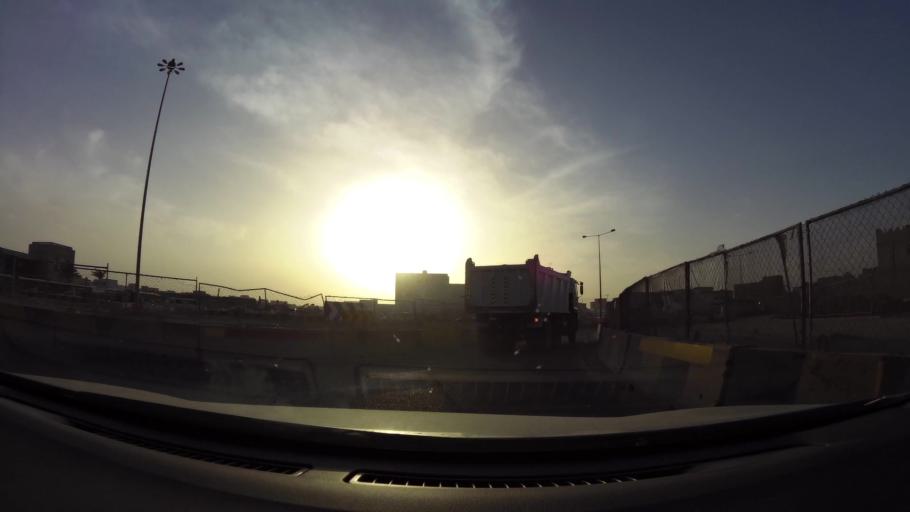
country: QA
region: Al Wakrah
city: Al Wakrah
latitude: 25.1516
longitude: 51.5944
